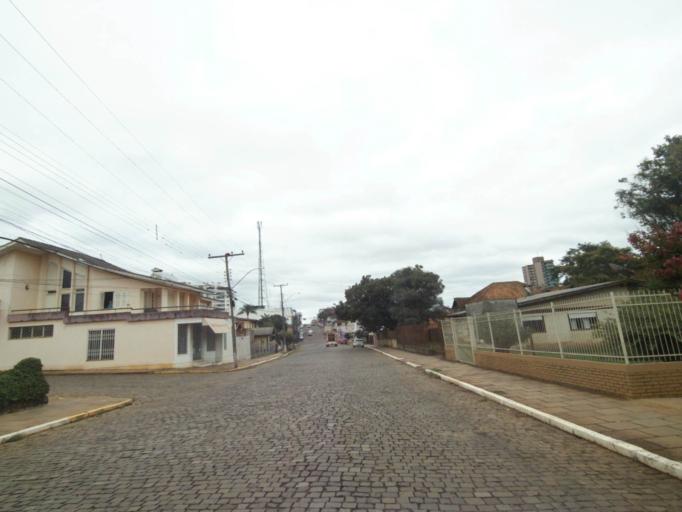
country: BR
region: Rio Grande do Sul
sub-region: Lagoa Vermelha
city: Lagoa Vermelha
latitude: -28.2072
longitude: -51.5231
